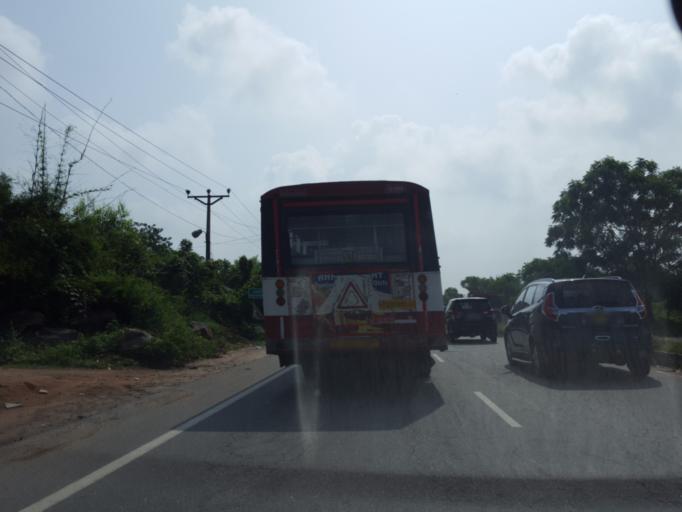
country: IN
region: Telangana
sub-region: Rangareddi
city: Ghatkesar
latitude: 17.3060
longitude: 78.7277
